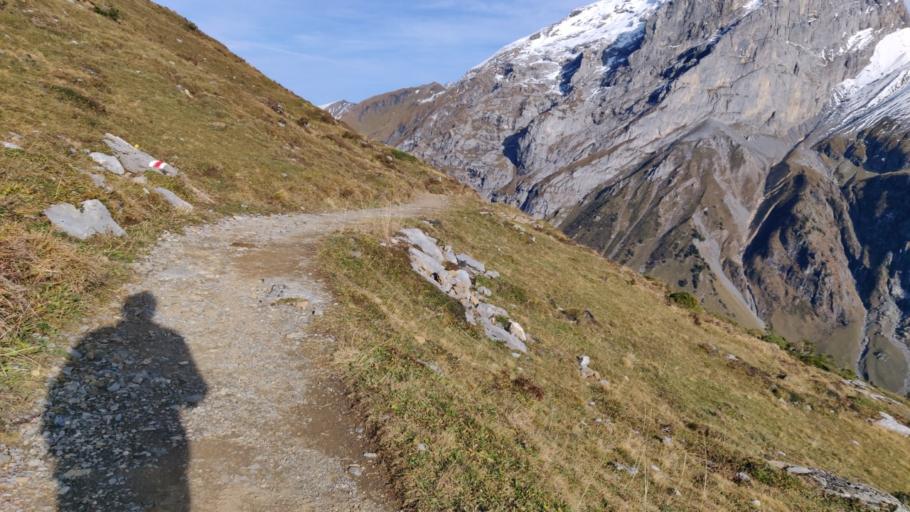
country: CH
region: Obwalden
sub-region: Obwalden
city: Engelberg
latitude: 46.8026
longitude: 8.4779
